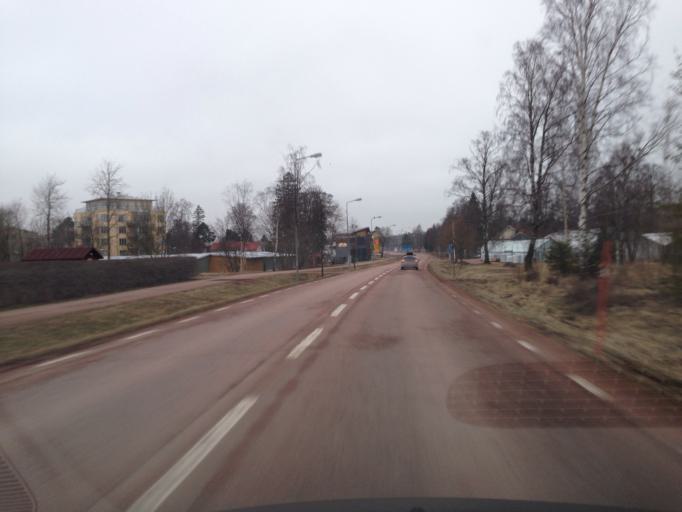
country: AX
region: Mariehamns stad
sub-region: Mariehamn
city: Mariehamn
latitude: 60.1085
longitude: 19.9306
